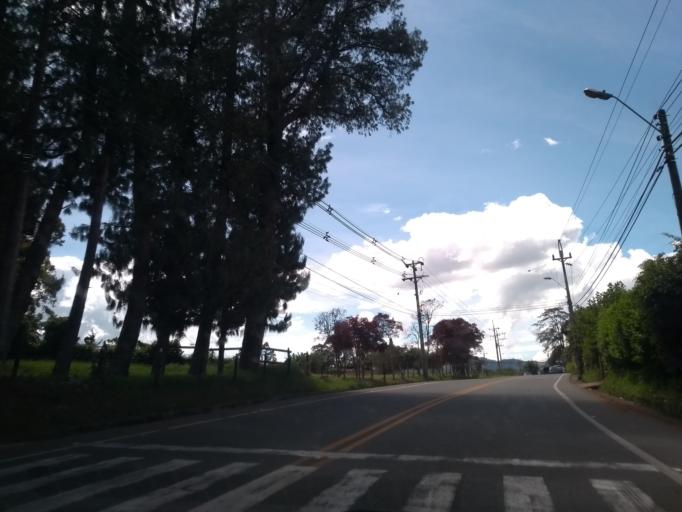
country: CO
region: Antioquia
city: La Ceja
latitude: 6.0504
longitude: -75.3919
